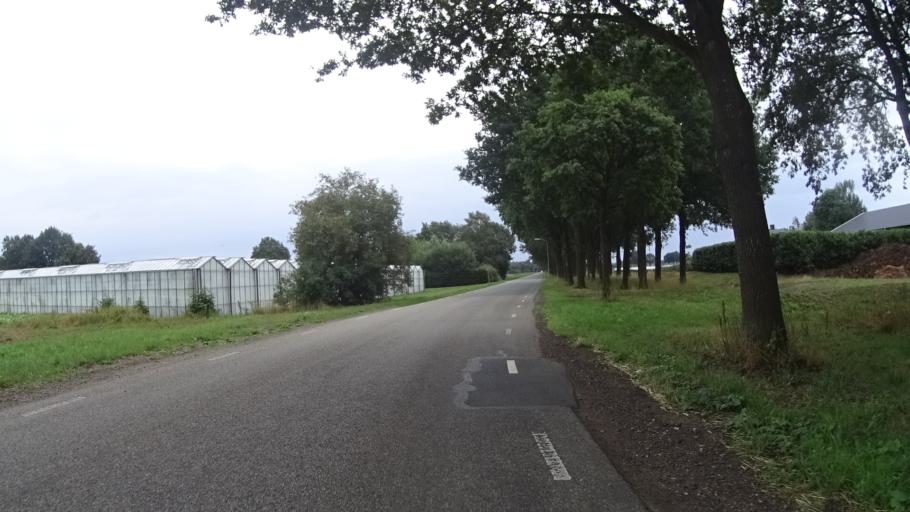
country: NL
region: Groningen
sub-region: Gemeente Slochteren
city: Slochteren
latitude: 53.1934
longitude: 6.8428
